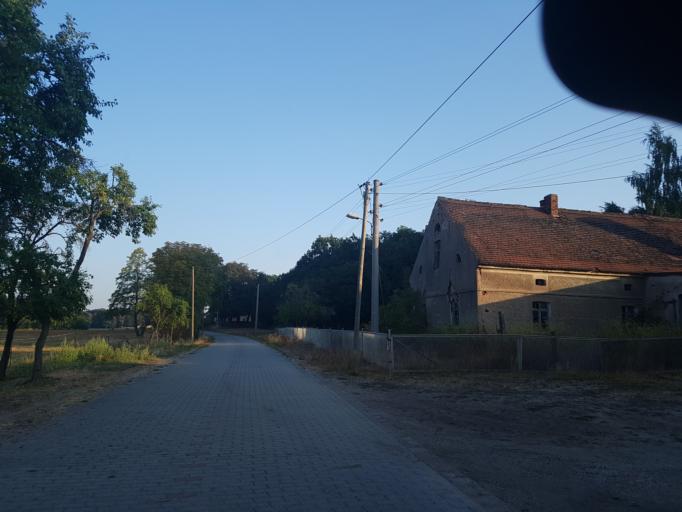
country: DE
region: Brandenburg
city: Falkenberg
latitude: 51.6437
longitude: 13.2936
